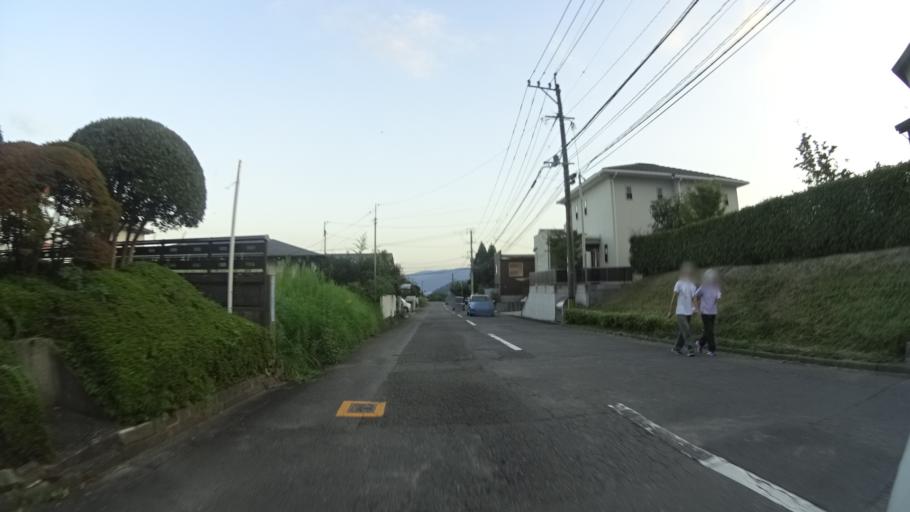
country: JP
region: Oita
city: Beppu
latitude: 33.3177
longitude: 131.4845
